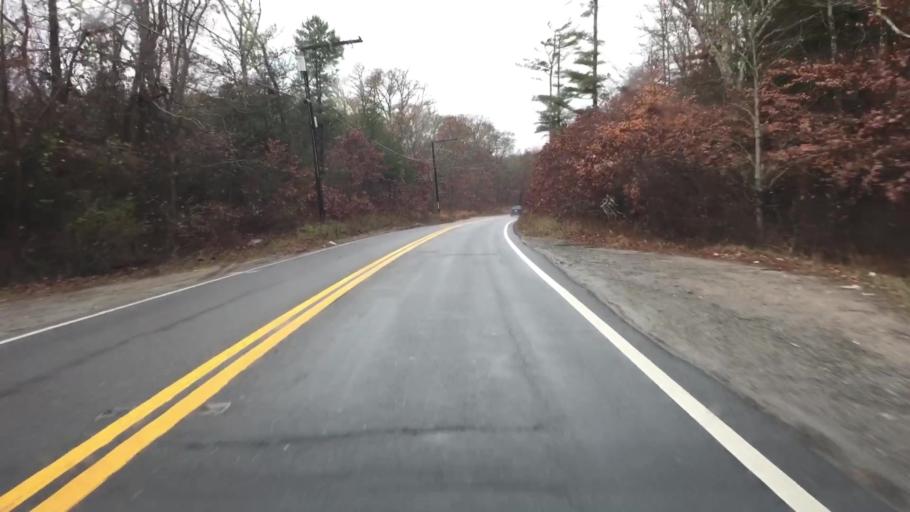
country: US
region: Massachusetts
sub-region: Barnstable County
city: Falmouth
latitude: 41.5745
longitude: -70.6227
